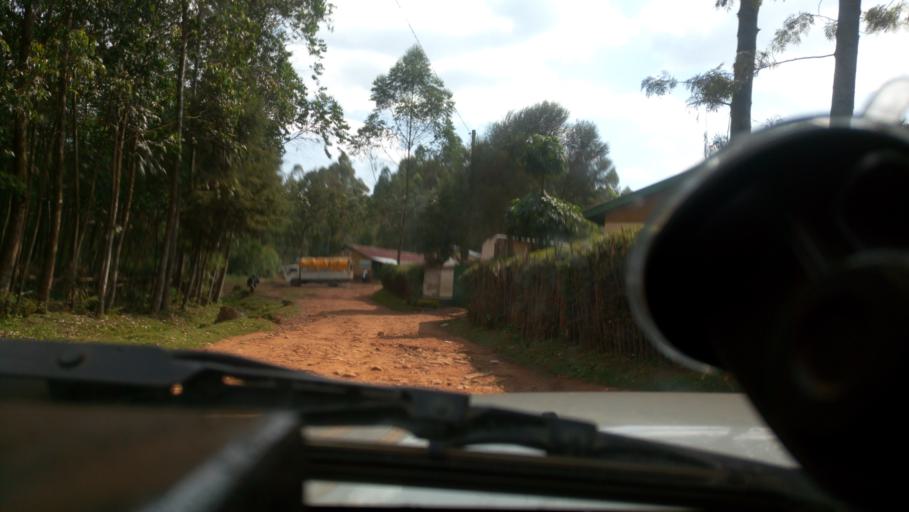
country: KE
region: Nyamira District
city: Nyamira
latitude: -0.5815
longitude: 35.0118
